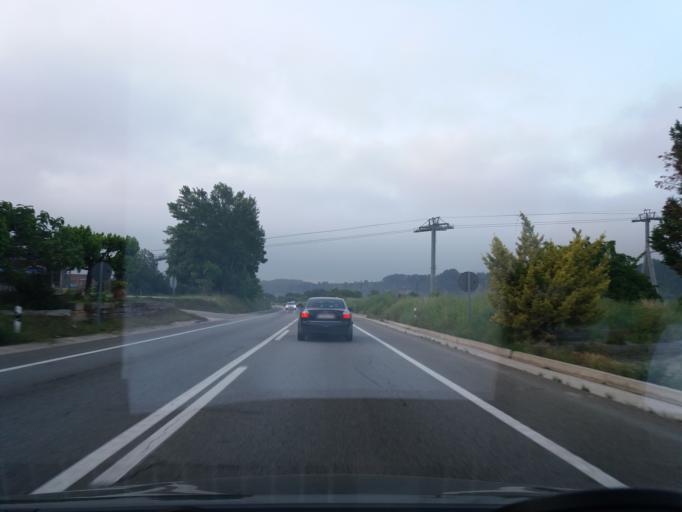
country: ES
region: Catalonia
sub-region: Provincia de Barcelona
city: Olesa de Montserrat
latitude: 41.5409
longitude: 1.8874
